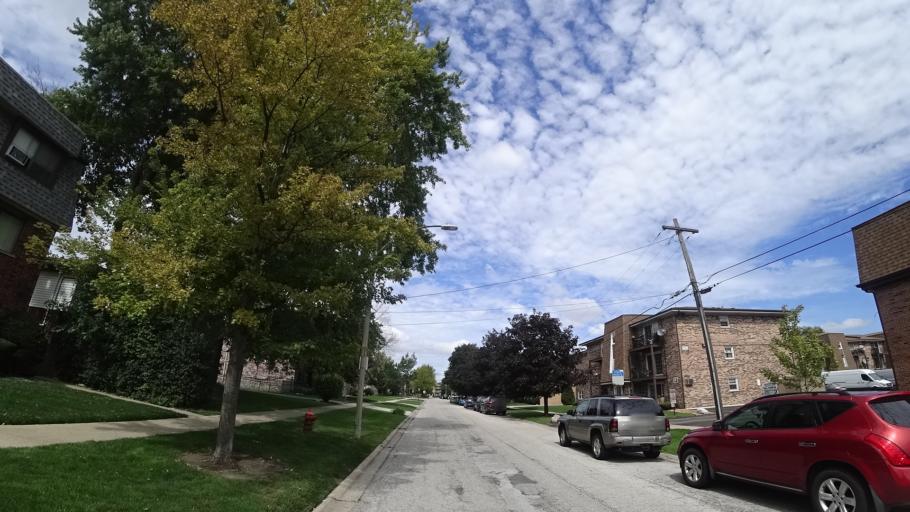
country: US
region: Illinois
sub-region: Cook County
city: Chicago Ridge
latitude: 41.7128
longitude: -87.7962
